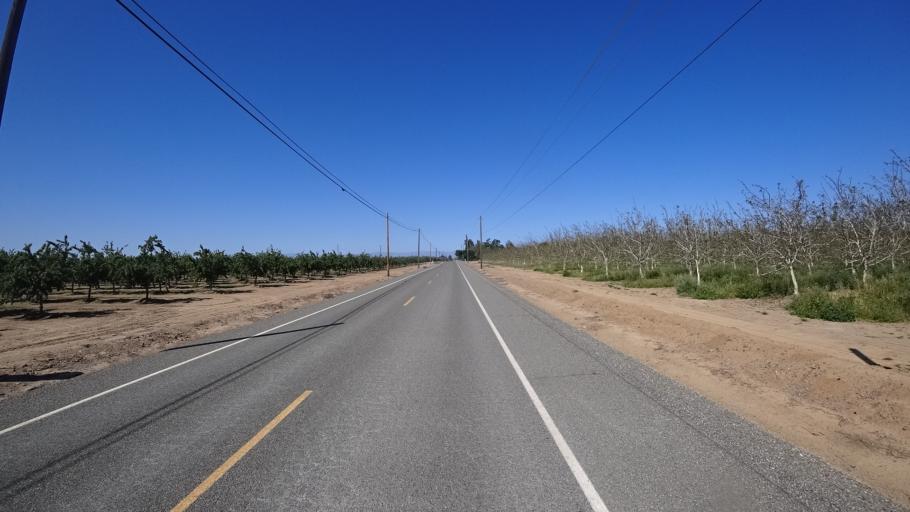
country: US
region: California
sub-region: Glenn County
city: Orland
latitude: 39.7105
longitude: -122.1201
